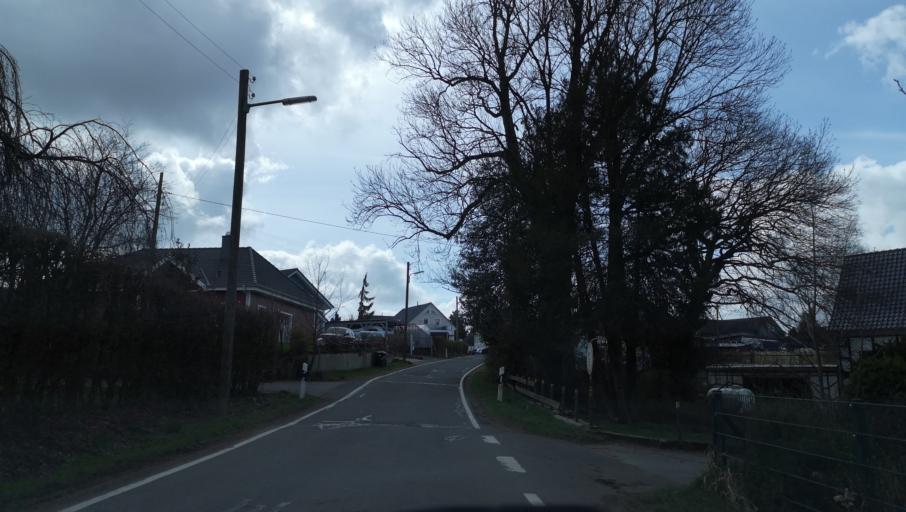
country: DE
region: North Rhine-Westphalia
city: Radevormwald
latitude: 51.2355
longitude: 7.3854
